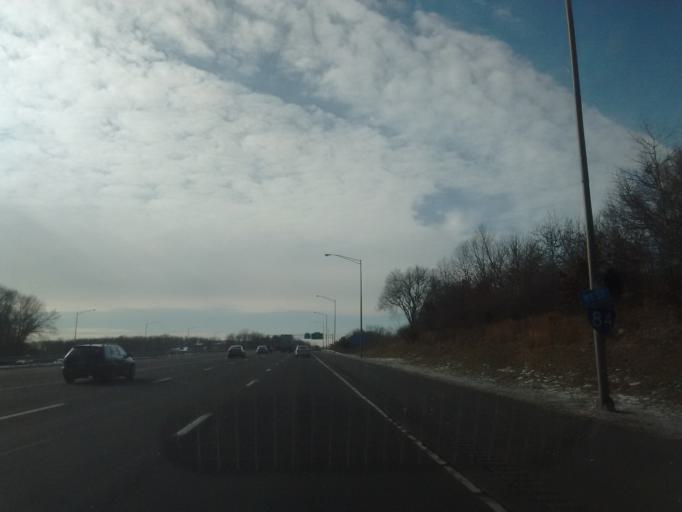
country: US
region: Connecticut
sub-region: Hartford County
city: Manchester
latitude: 41.8078
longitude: -72.5316
